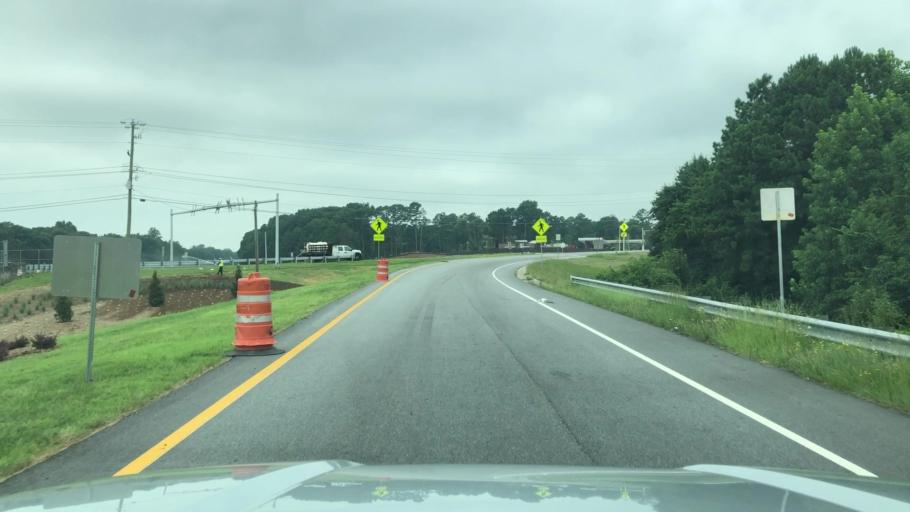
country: US
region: Georgia
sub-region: Cobb County
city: Mableton
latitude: 33.7745
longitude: -84.5596
